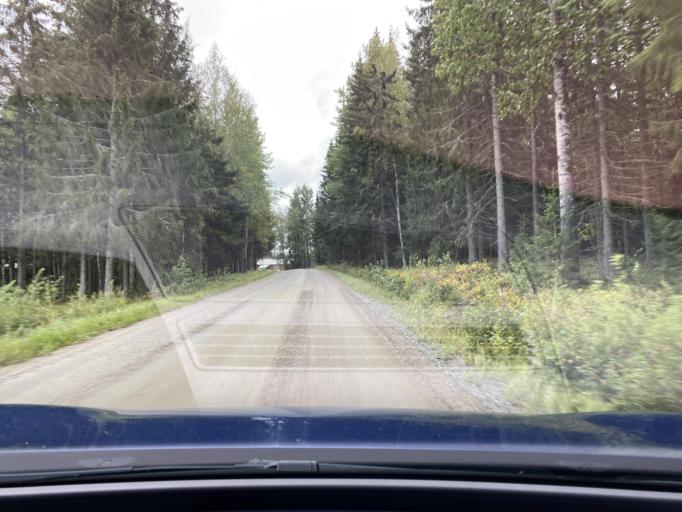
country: FI
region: Pirkanmaa
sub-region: Lounais-Pirkanmaa
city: Punkalaidun
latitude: 61.2187
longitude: 23.1658
